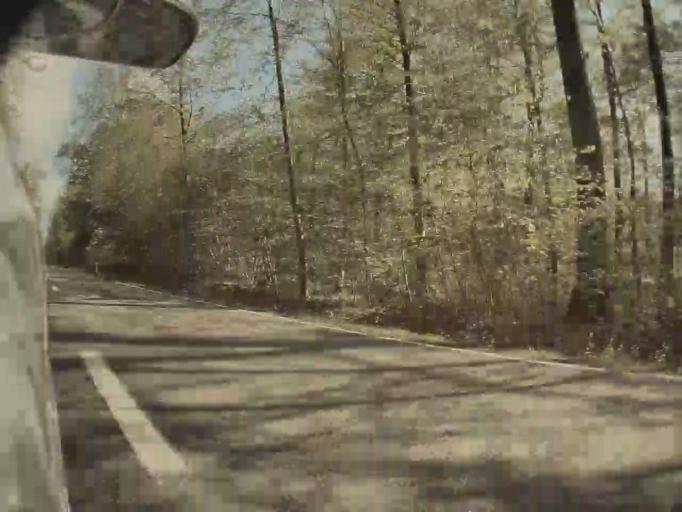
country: BE
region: Wallonia
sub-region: Province du Luxembourg
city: Tellin
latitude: 50.0393
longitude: 5.2082
